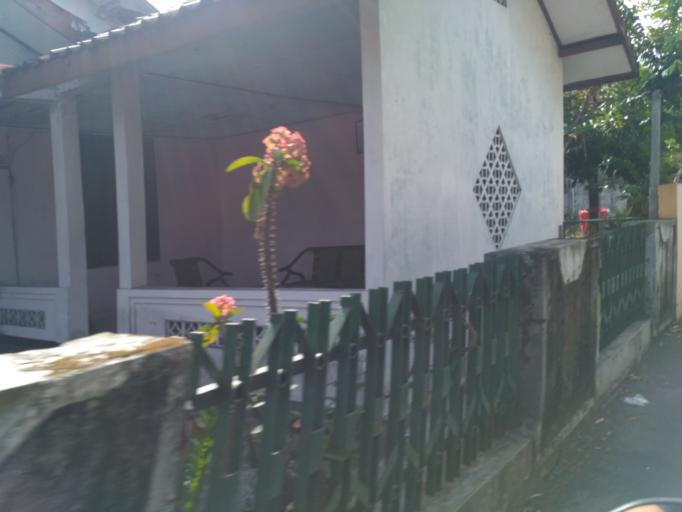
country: ID
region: Daerah Istimewa Yogyakarta
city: Depok
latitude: -7.7832
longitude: 110.4317
